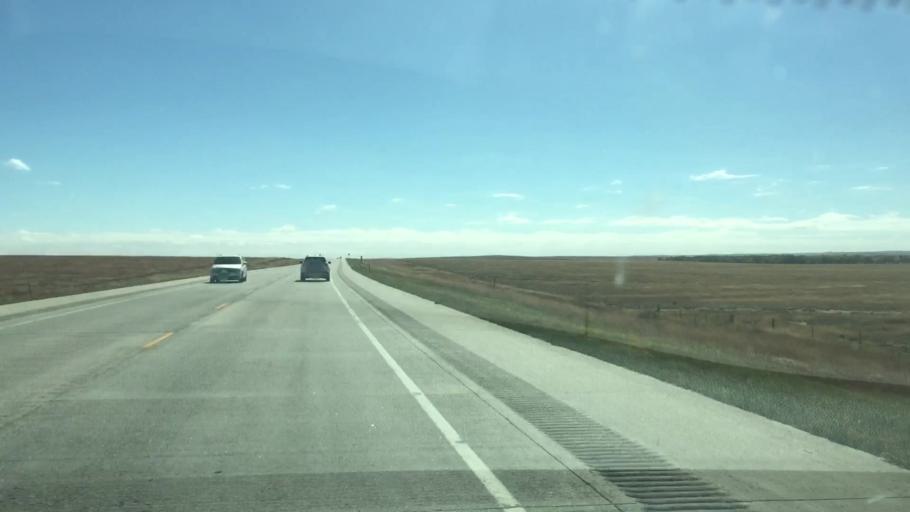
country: US
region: Colorado
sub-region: Lincoln County
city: Hugo
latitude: 39.1903
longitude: -103.5609
